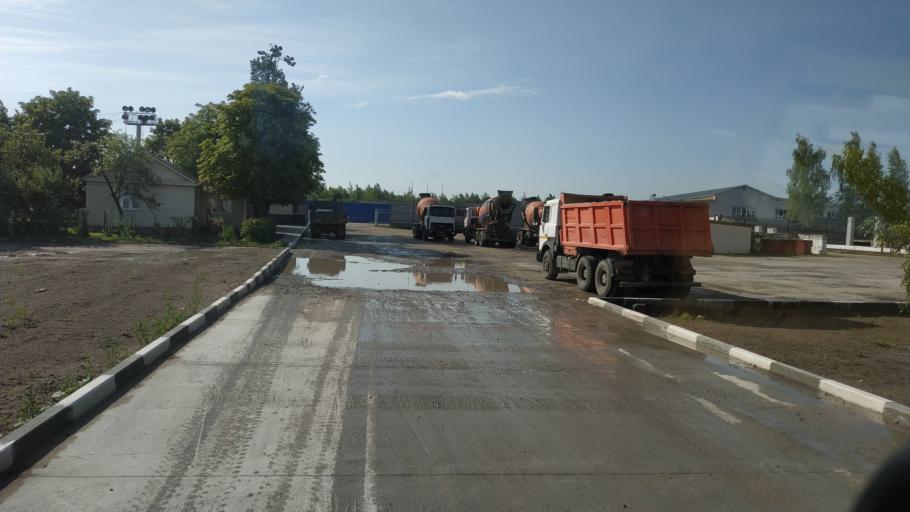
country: BY
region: Mogilev
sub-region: Mahilyowski Rayon
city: Veyno
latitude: 53.8385
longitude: 30.3850
